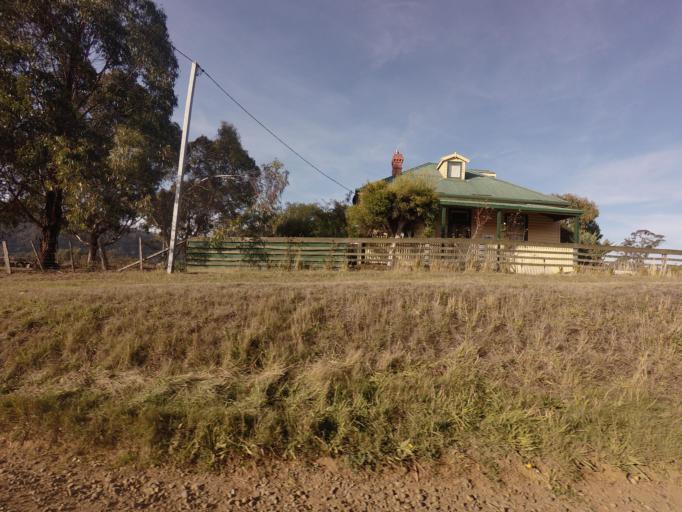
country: AU
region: Tasmania
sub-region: Brighton
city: Bridgewater
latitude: -42.4788
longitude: 147.3845
